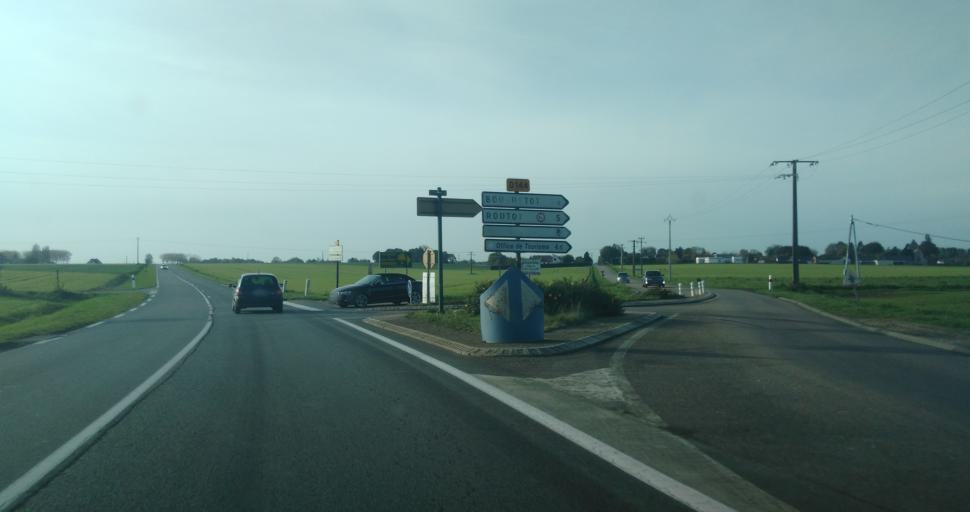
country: FR
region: Haute-Normandie
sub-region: Departement de l'Eure
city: Bourg-Achard
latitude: 49.3575
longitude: 0.7908
